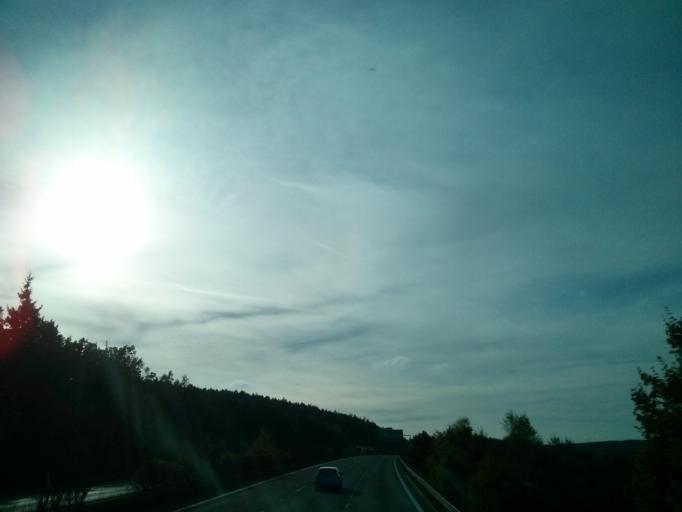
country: CZ
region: Plzensky
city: Dysina
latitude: 49.7405
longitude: 13.5353
